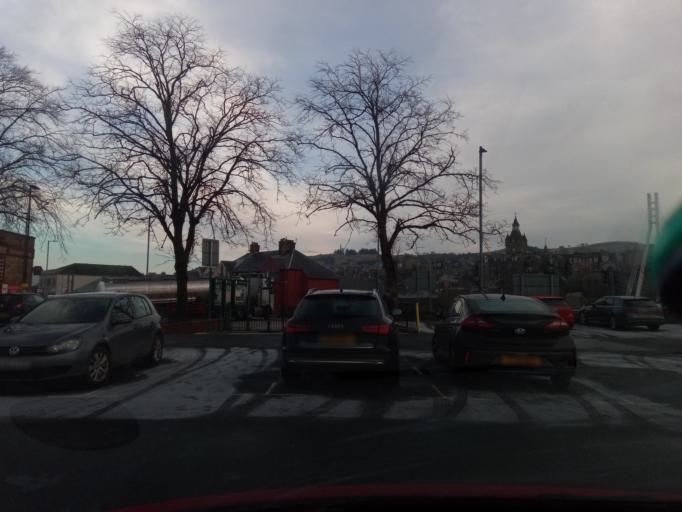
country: GB
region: Scotland
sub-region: The Scottish Borders
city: Hawick
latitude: 55.4233
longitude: -2.7909
